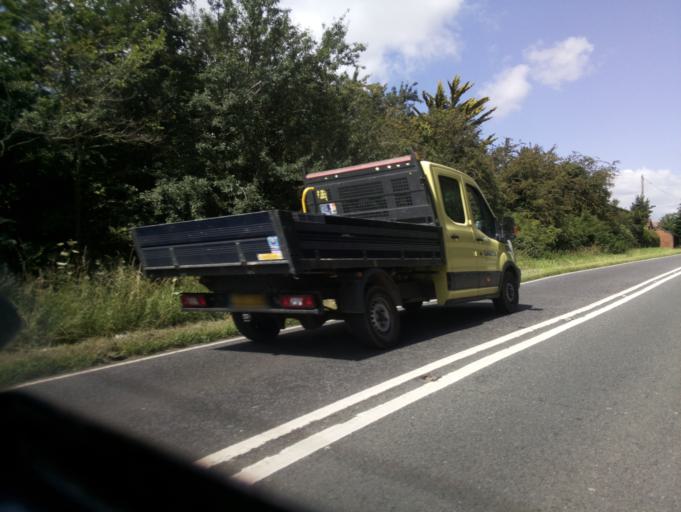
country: GB
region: England
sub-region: Buckinghamshire
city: Aylesbury
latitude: 51.8394
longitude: -0.8179
